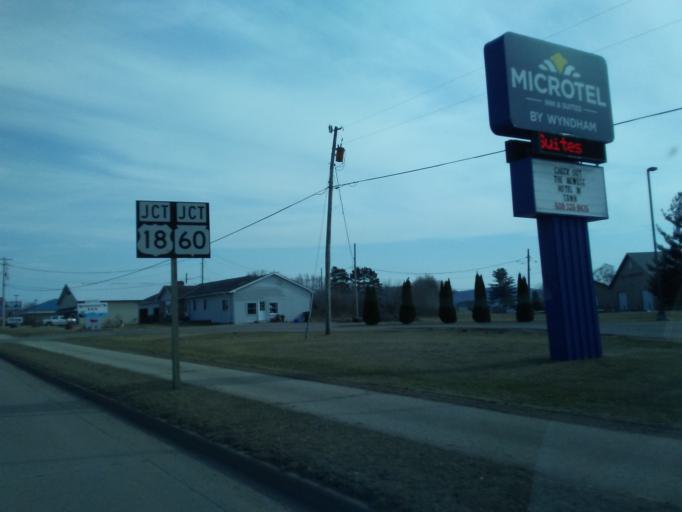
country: US
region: Wisconsin
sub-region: Crawford County
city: Prairie du Chien
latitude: 43.0303
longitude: -91.1306
